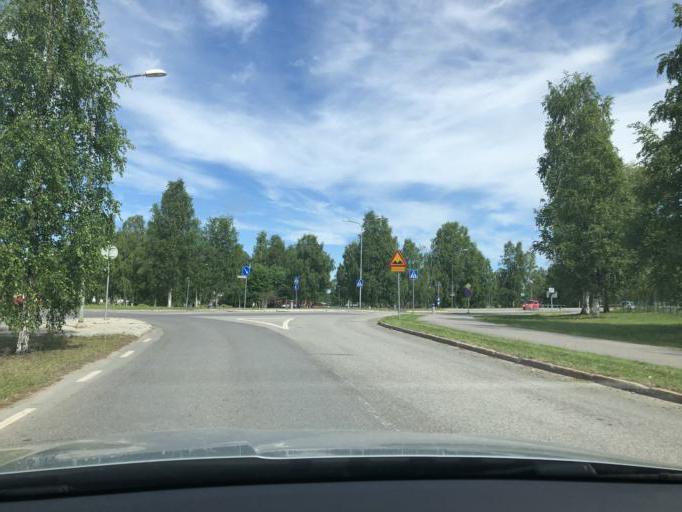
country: SE
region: Norrbotten
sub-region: Pitea Kommun
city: Pitea
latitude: 65.3146
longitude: 21.4922
